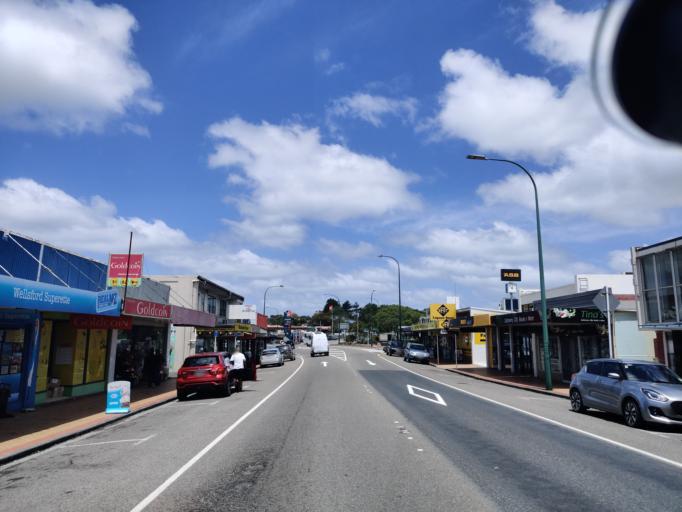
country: NZ
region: Auckland
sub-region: Auckland
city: Wellsford
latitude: -36.2951
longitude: 174.5236
